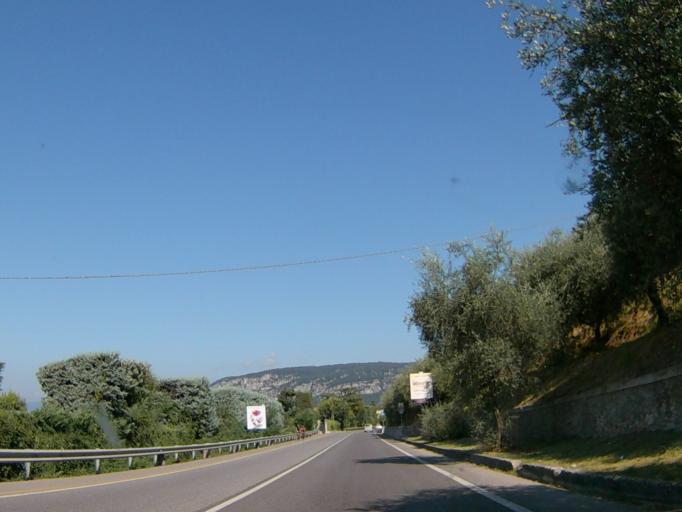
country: IT
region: Veneto
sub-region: Provincia di Verona
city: Garda
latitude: 45.5597
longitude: 10.7167
